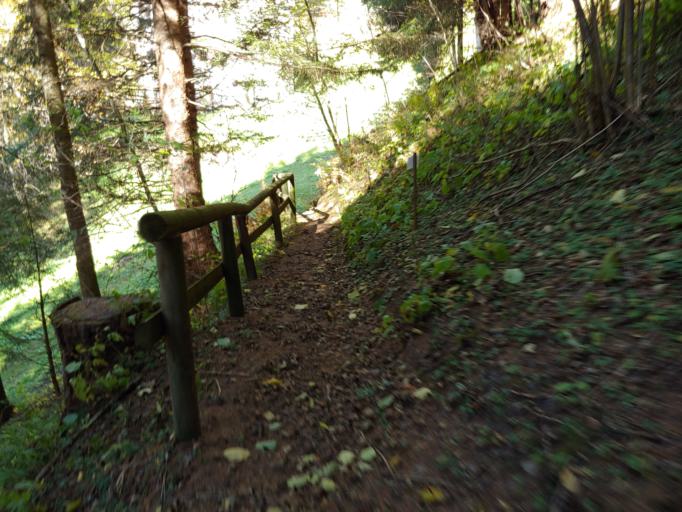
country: IT
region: Veneto
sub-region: Provincia di Belluno
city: Lozzo di Cadore
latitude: 46.4904
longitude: 12.4345
